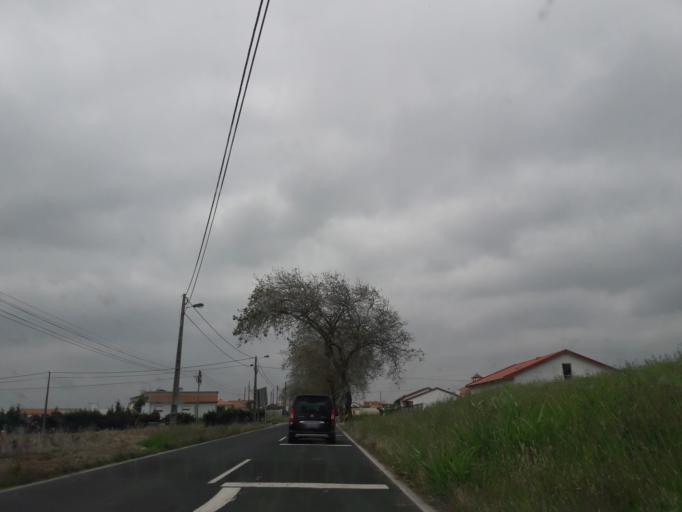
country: PT
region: Leiria
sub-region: Peniche
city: Atouguia da Baleia
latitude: 39.3329
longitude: -9.2610
